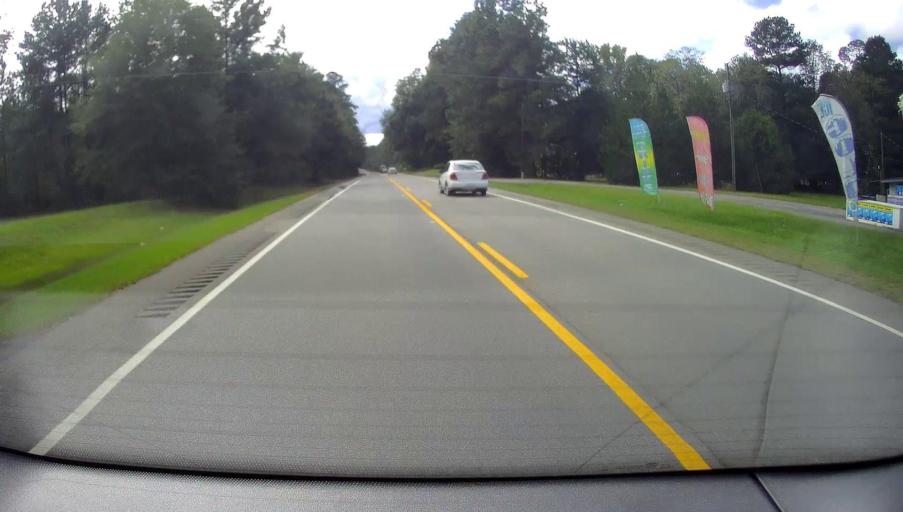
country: US
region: Georgia
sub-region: Baldwin County
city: Milledgeville
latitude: 33.0230
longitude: -83.3318
